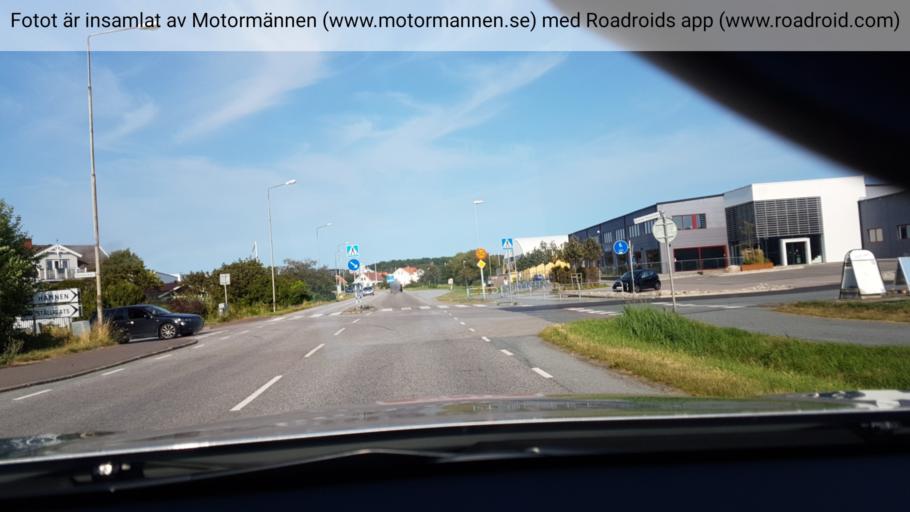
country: SE
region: Vaestra Goetaland
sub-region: Ockero Kommun
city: Hono
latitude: 57.6840
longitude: 11.6506
